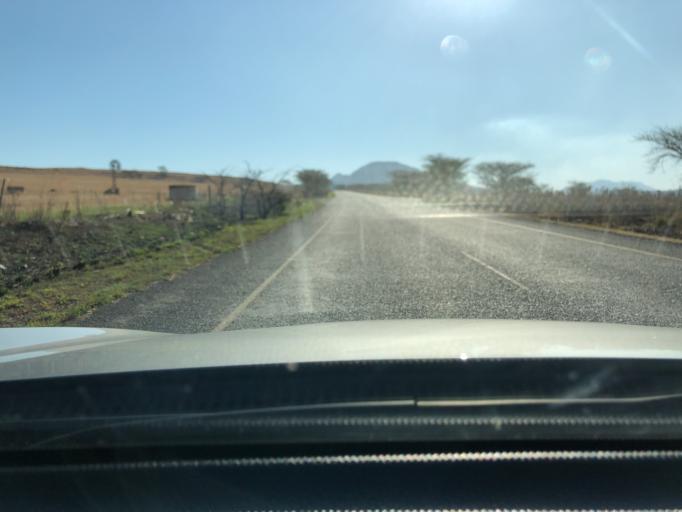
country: ZA
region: KwaZulu-Natal
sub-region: uThukela District Municipality
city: Ekuvukeni
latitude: -28.4031
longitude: 29.9426
